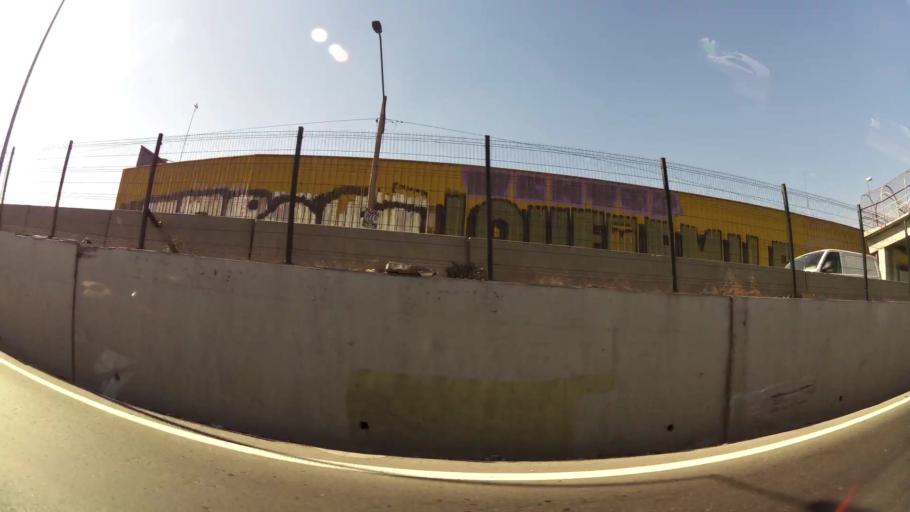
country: CL
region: Santiago Metropolitan
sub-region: Provincia de Maipo
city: San Bernardo
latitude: -33.5324
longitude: -70.6798
